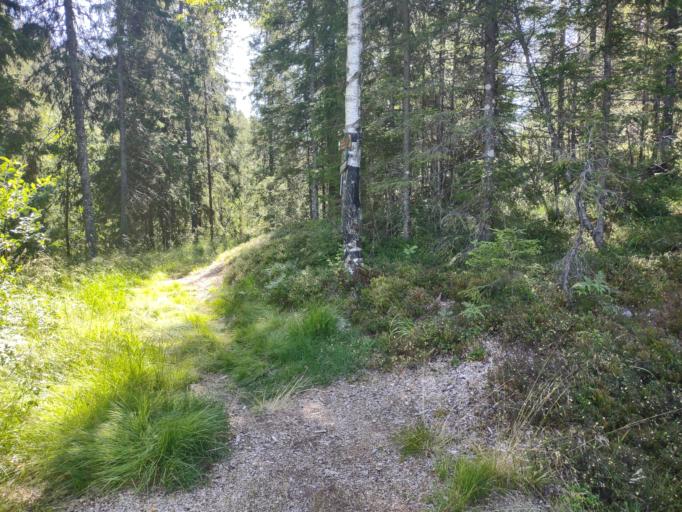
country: NO
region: Akershus
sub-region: Raelingen
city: Fjerdingby
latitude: 59.8858
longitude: 11.0491
